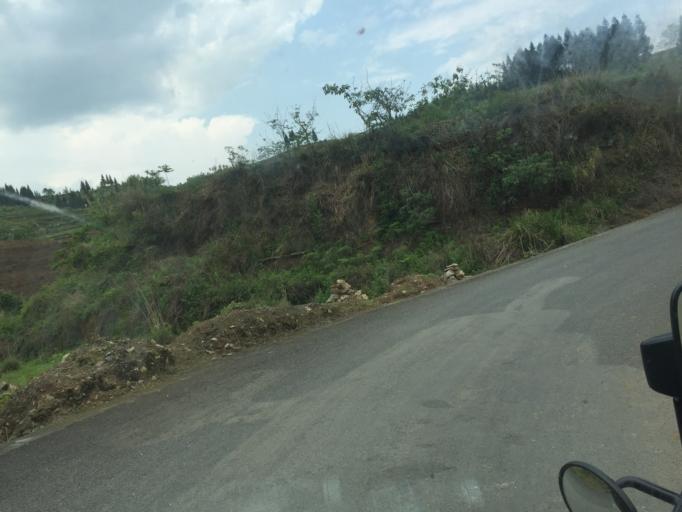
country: CN
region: Guangxi Zhuangzu Zizhiqu
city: Xinzhou
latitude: 25.6593
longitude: 105.2367
